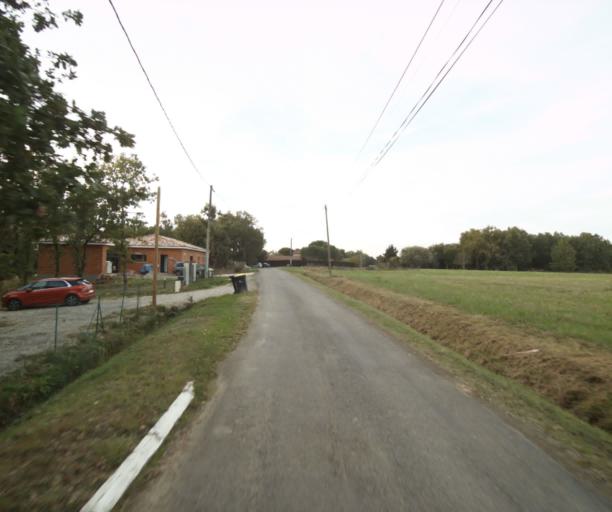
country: FR
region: Midi-Pyrenees
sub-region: Departement du Tarn-et-Garonne
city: Pompignan
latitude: 43.8237
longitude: 1.3148
